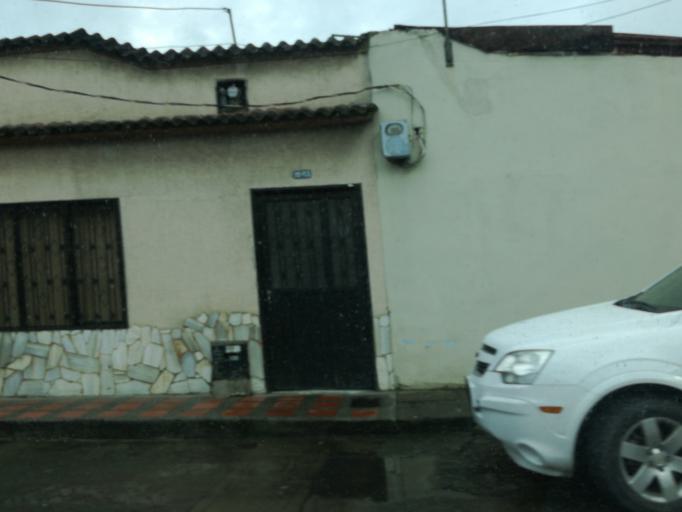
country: CO
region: Valle del Cauca
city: Palmira
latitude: 3.5188
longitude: -76.3039
